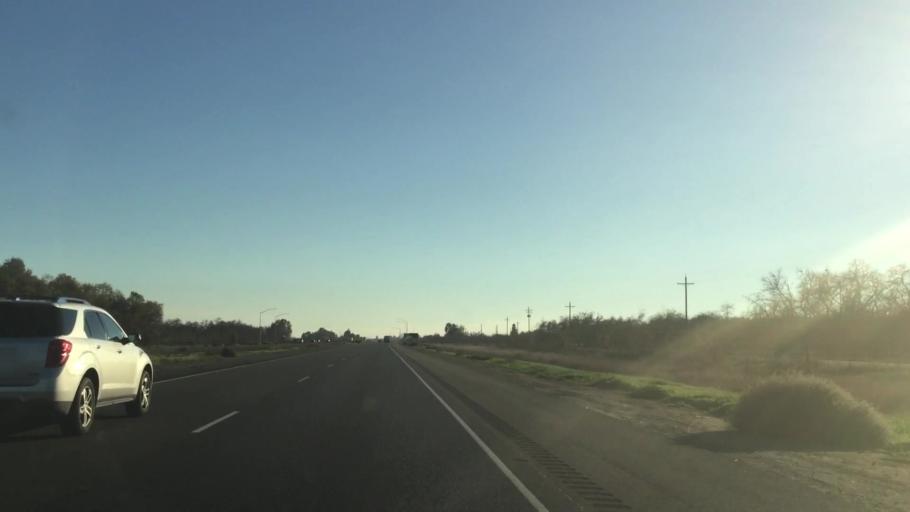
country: US
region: California
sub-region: Yuba County
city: Plumas Lake
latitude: 38.9601
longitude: -121.5439
